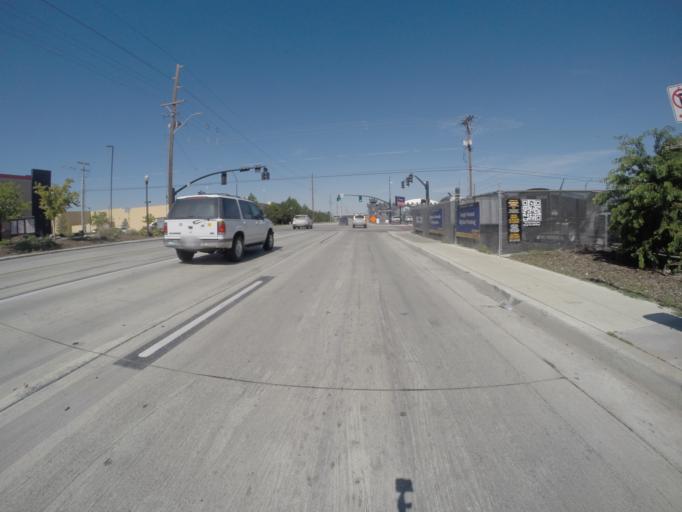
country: US
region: Utah
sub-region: Salt Lake County
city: Salt Lake City
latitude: 40.7417
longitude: -111.8990
